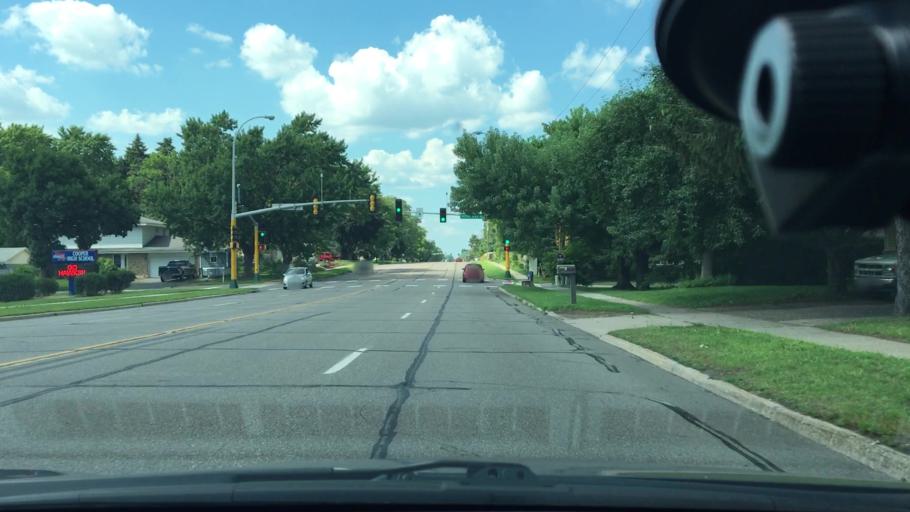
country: US
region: Minnesota
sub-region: Hennepin County
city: New Hope
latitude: 45.0395
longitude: -93.3803
